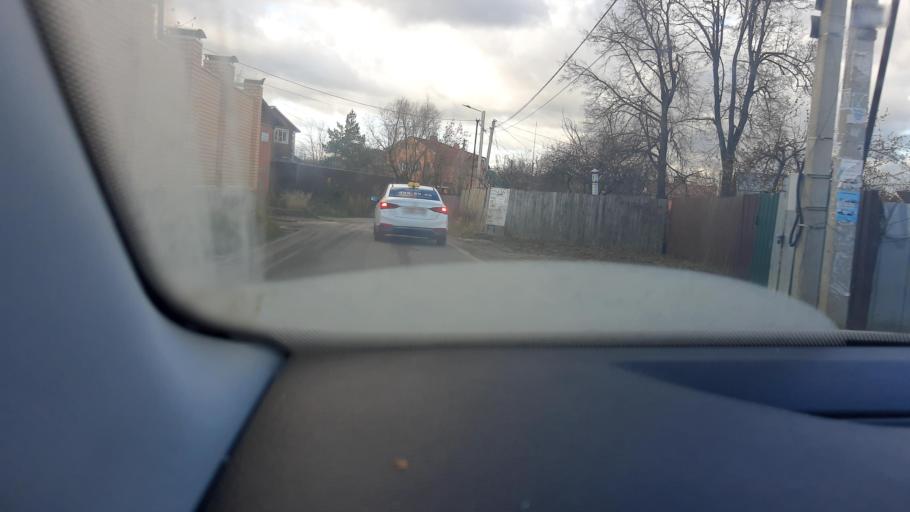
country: RU
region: Moscow
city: Annino
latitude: 55.5556
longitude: 37.6242
